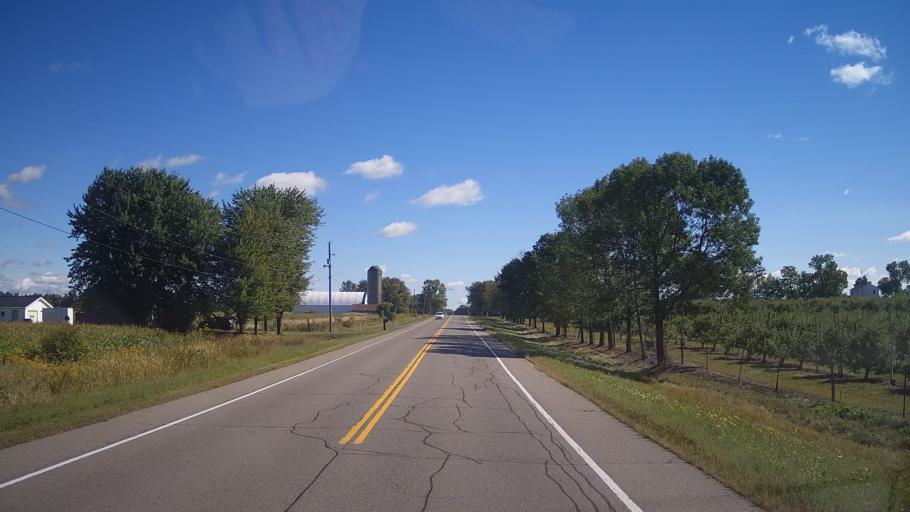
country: US
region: New York
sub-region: St. Lawrence County
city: Ogdensburg
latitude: 44.9427
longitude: -75.3015
